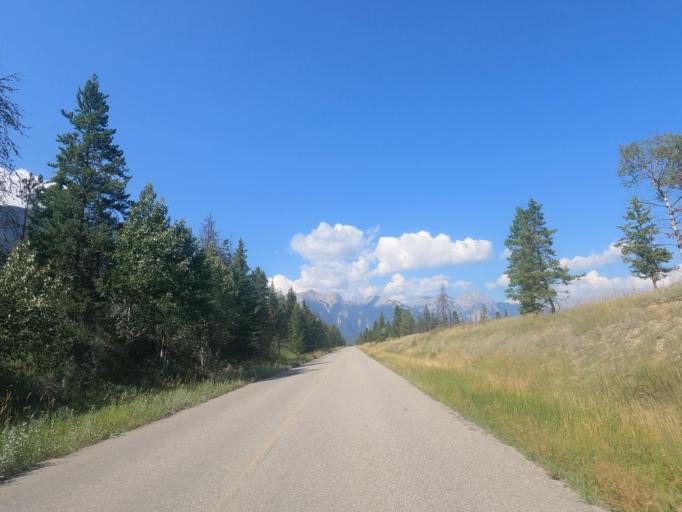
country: CA
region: Alberta
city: Jasper Park Lodge
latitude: 52.9740
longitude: -118.0625
